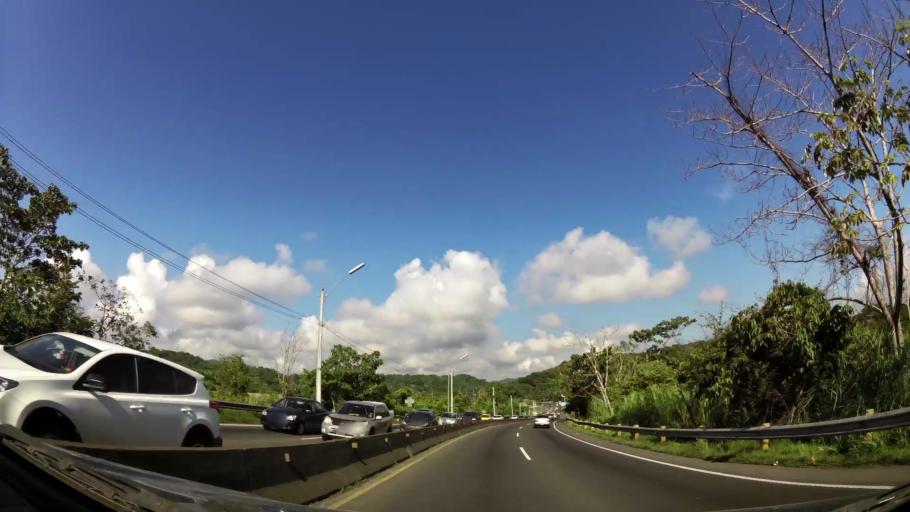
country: PA
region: Panama
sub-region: Distrito de Panama
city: Ancon
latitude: 8.9410
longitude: -79.5742
